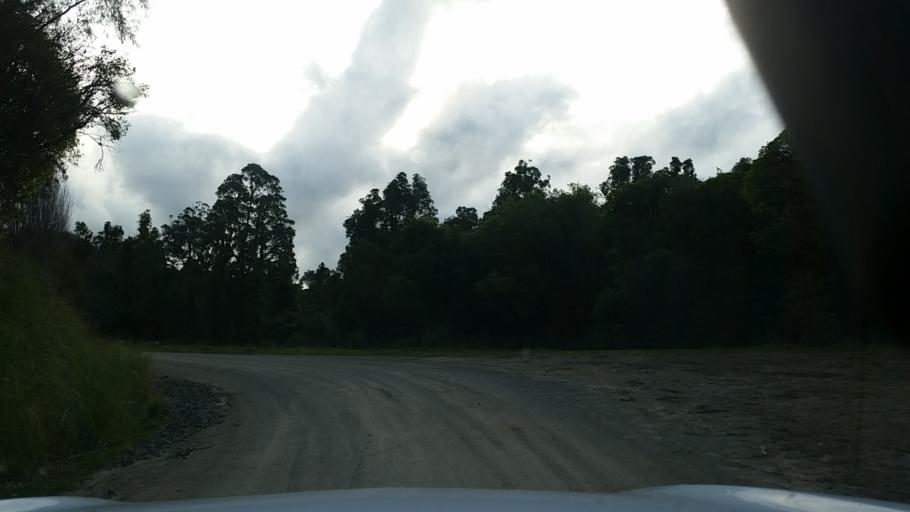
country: NZ
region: Taranaki
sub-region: South Taranaki District
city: Patea
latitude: -39.5563
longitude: 174.8029
